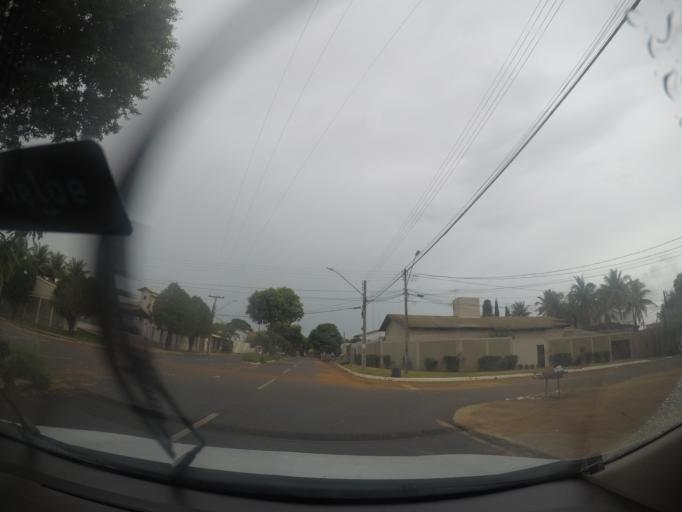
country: BR
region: Goias
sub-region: Goiania
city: Goiania
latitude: -16.6494
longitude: -49.2320
